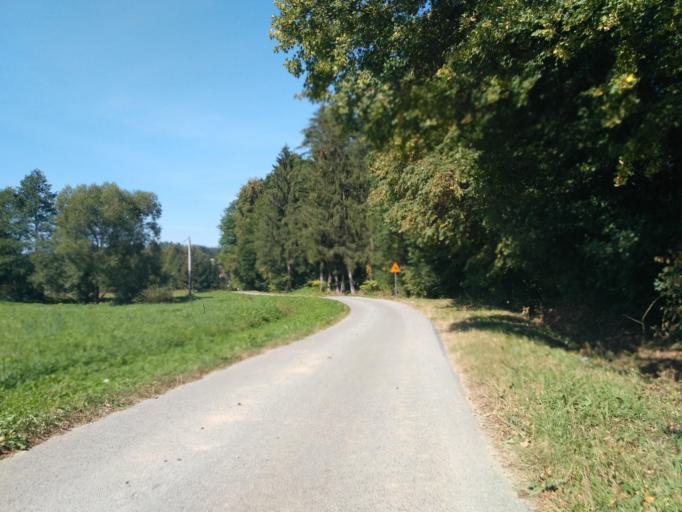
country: PL
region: Subcarpathian Voivodeship
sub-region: Powiat brzozowski
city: Niebocko
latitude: 49.6396
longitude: 22.1338
